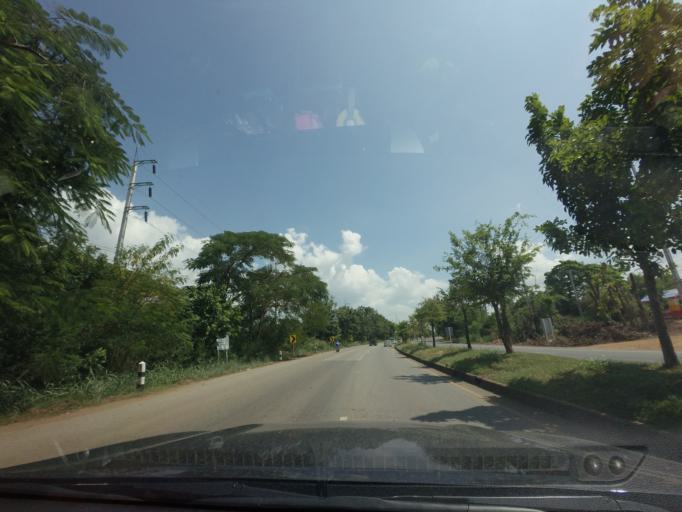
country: TH
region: Phetchabun
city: Nong Phai
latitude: 16.0763
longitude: 101.0650
